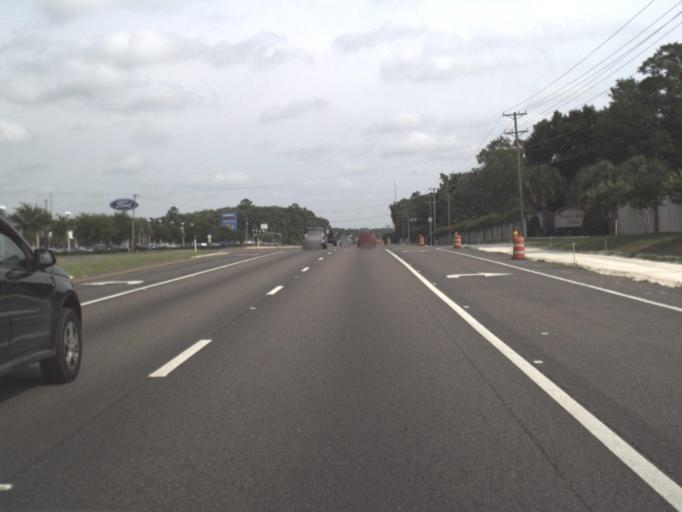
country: US
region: Florida
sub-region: Clay County
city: Green Cove Springs
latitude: 30.0146
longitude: -81.7010
